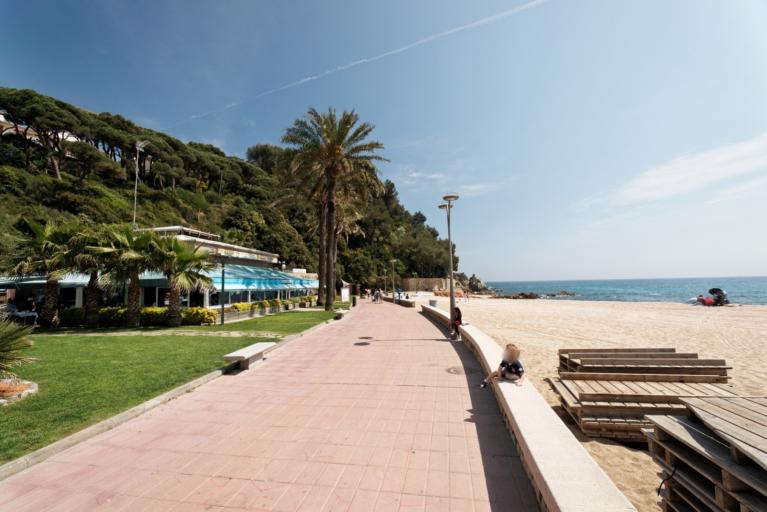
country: ES
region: Catalonia
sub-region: Provincia de Girona
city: Lloret de Mar
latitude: 41.6951
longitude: 2.8362
